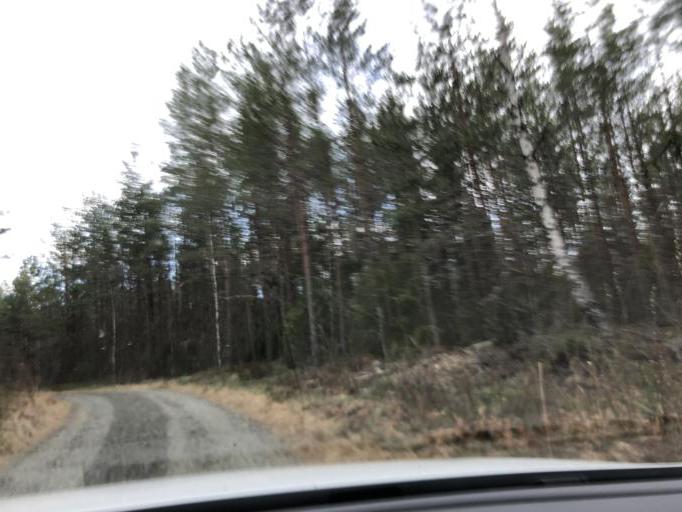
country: SE
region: Uppsala
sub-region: Heby Kommun
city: OEstervala
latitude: 60.3305
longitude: 17.1765
